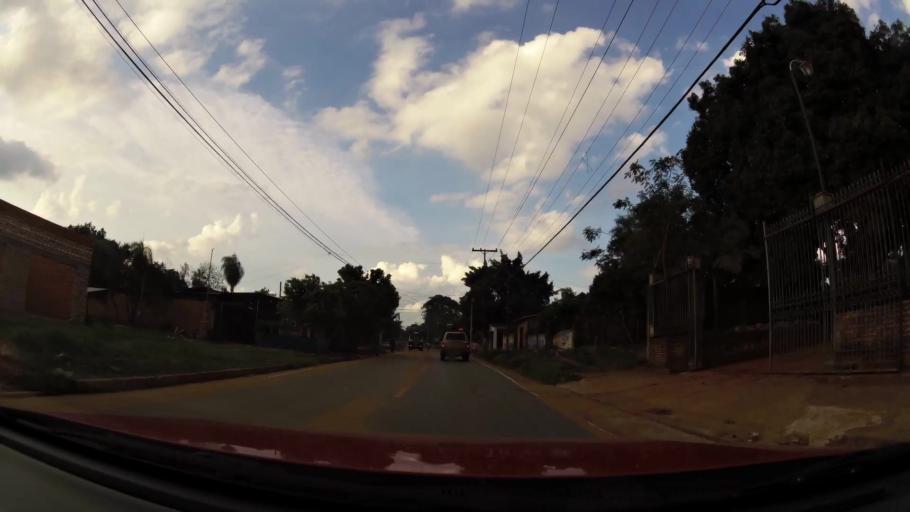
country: PY
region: Central
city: Nemby
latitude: -25.3701
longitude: -57.5423
